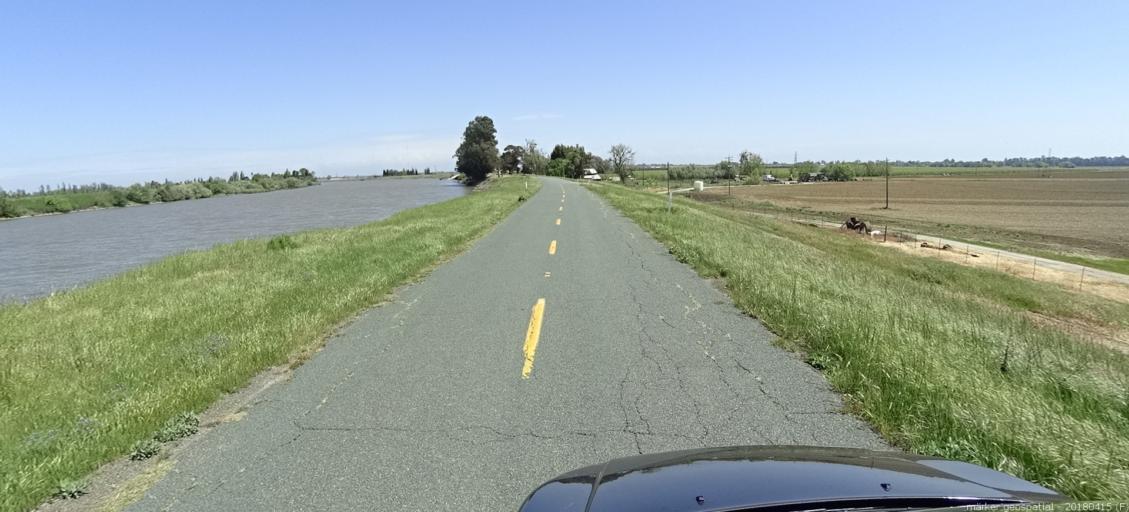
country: US
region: California
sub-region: Solano County
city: Rio Vista
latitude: 38.1924
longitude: -121.6233
